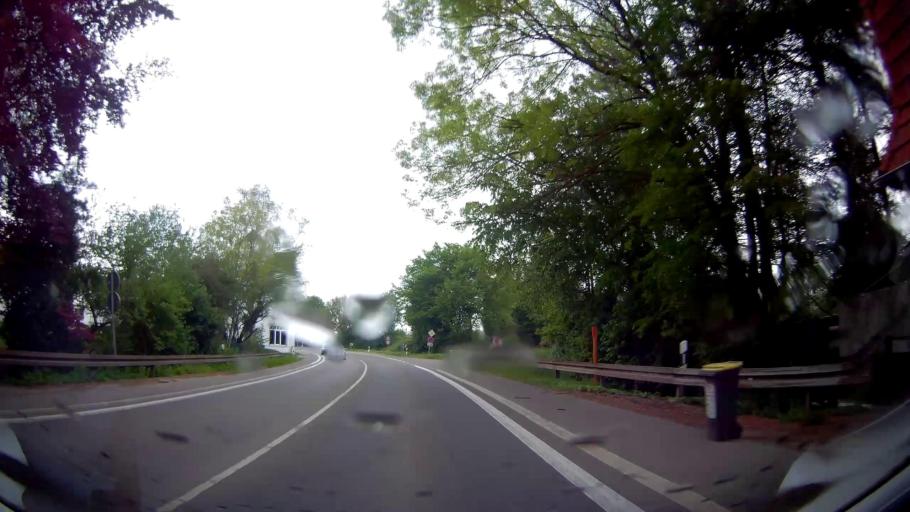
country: DE
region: North Rhine-Westphalia
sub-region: Regierungsbezirk Munster
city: Gladbeck
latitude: 51.5843
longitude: 6.9467
